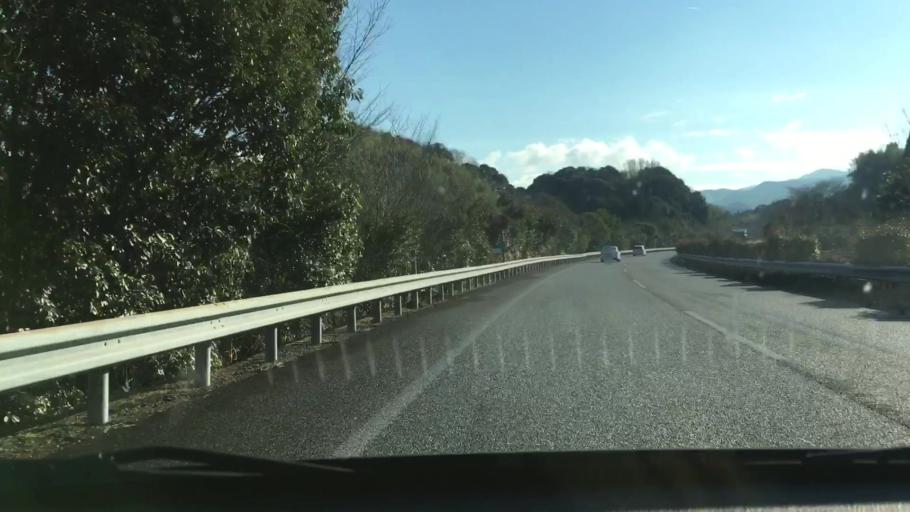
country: JP
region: Kumamoto
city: Hitoyoshi
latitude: 32.1950
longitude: 130.7779
